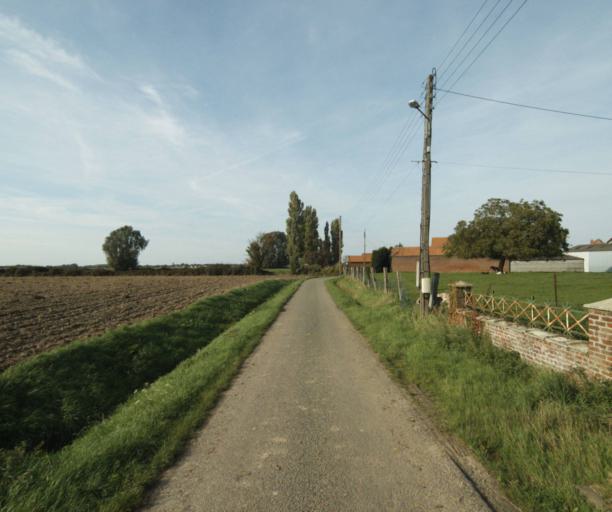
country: FR
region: Nord-Pas-de-Calais
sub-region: Departement du Nord
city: Fournes-en-Weppes
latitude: 50.5903
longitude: 2.8738
